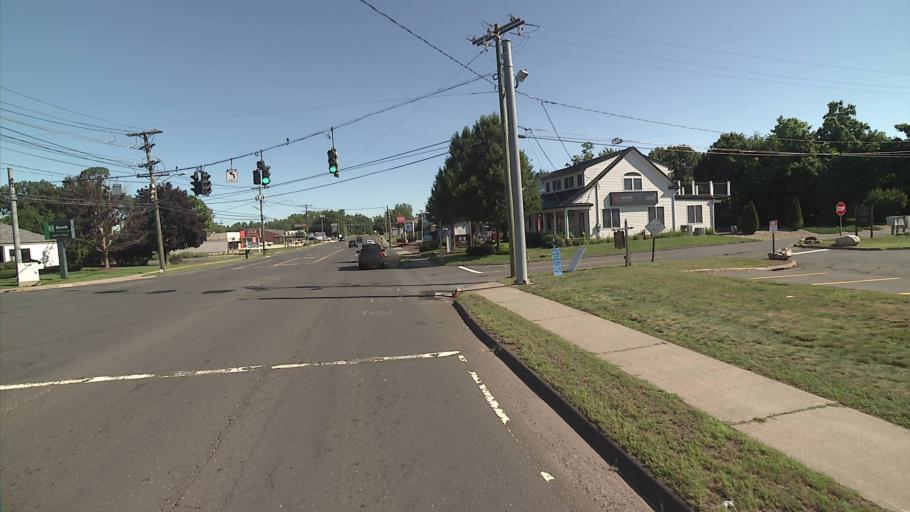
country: US
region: Connecticut
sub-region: Hartford County
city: Plainville
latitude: 41.6408
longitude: -72.8739
